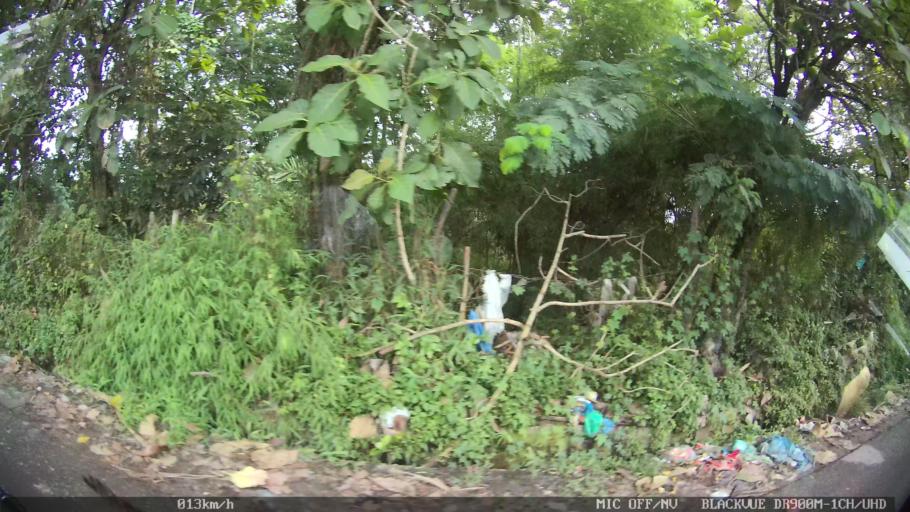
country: ID
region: North Sumatra
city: Medan
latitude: 3.6217
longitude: 98.7128
